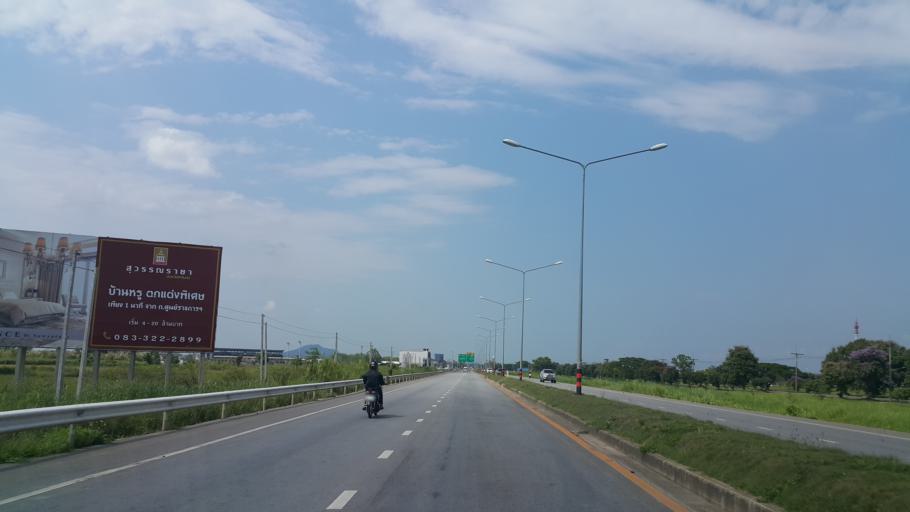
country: TH
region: Chiang Rai
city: Chiang Rai
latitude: 19.9489
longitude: 99.8736
